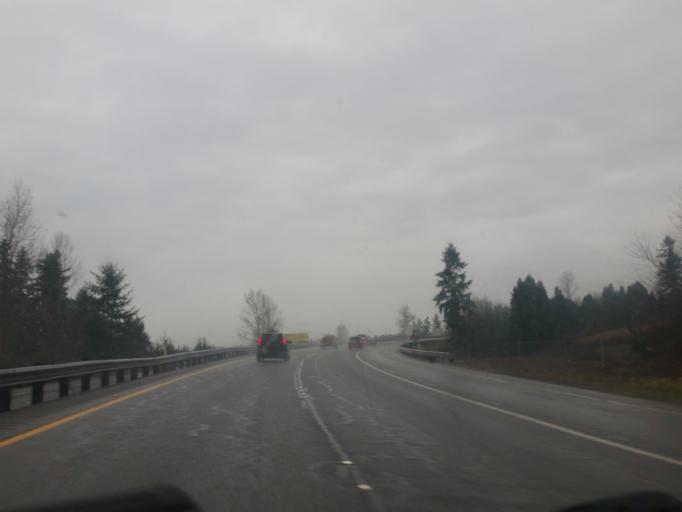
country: US
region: Washington
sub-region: Snohomish County
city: Maltby
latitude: 47.7920
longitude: -122.1369
